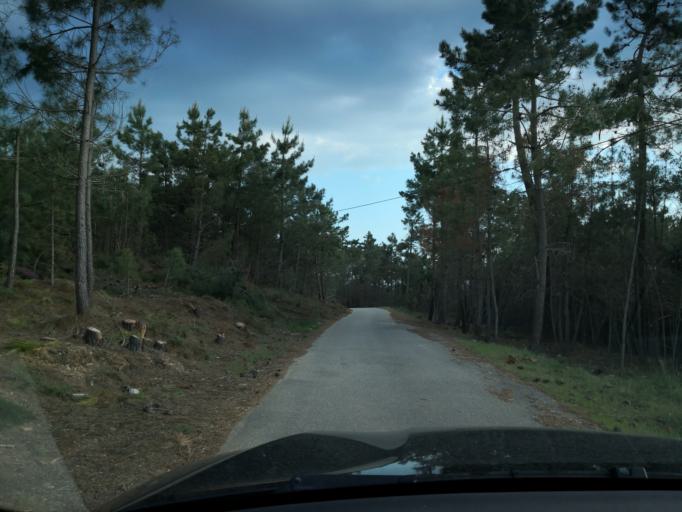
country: PT
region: Vila Real
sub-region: Sabrosa
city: Vilela
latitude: 41.2251
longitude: -7.6709
